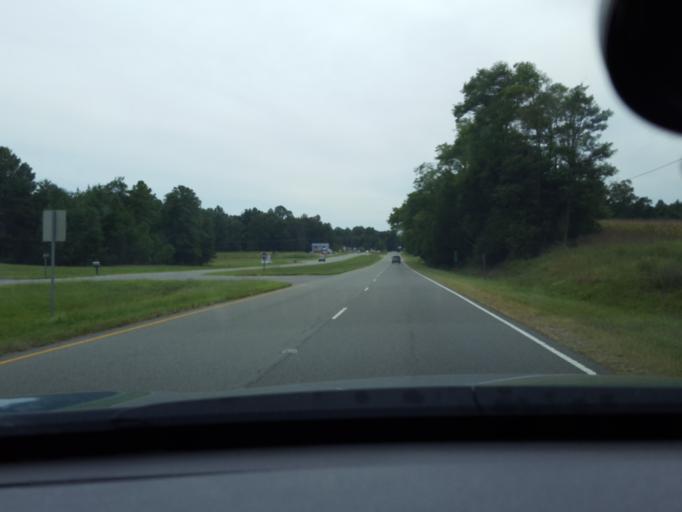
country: US
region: Virginia
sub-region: Caroline County
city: Bowling Green
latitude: 38.0665
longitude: -77.3328
